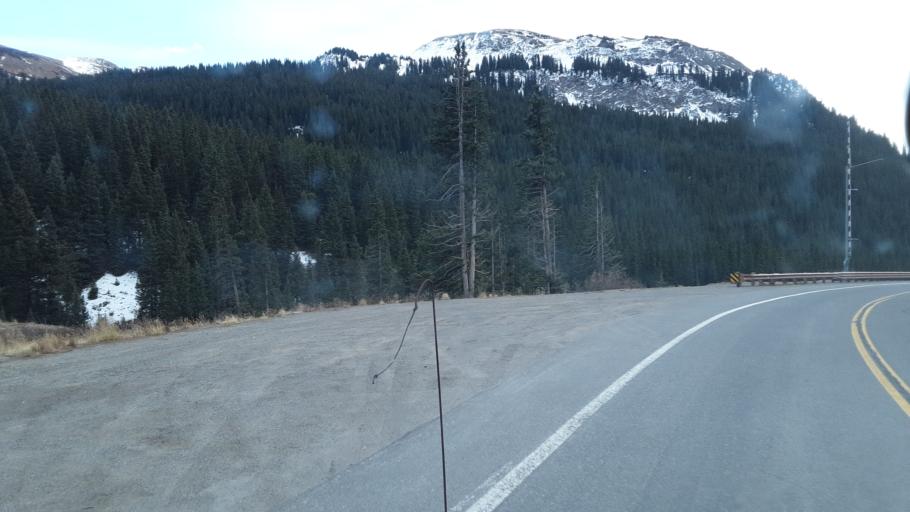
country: US
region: Colorado
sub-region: San Juan County
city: Silverton
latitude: 37.8882
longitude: -107.7192
